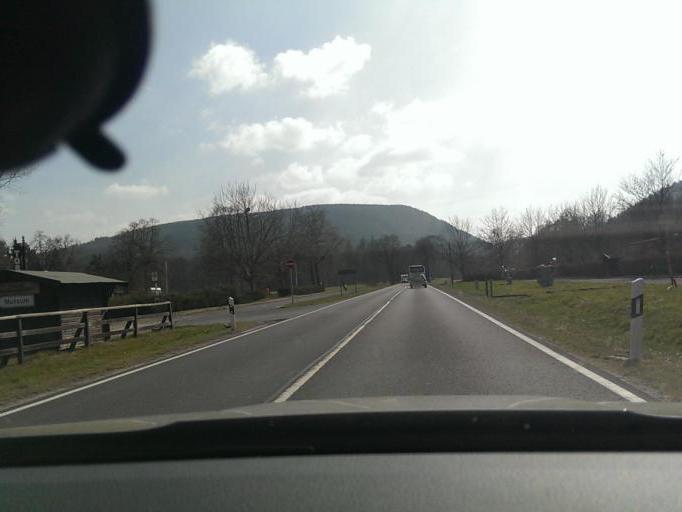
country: DE
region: Thuringia
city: Luisenthal
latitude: 50.8031
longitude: 10.7295
